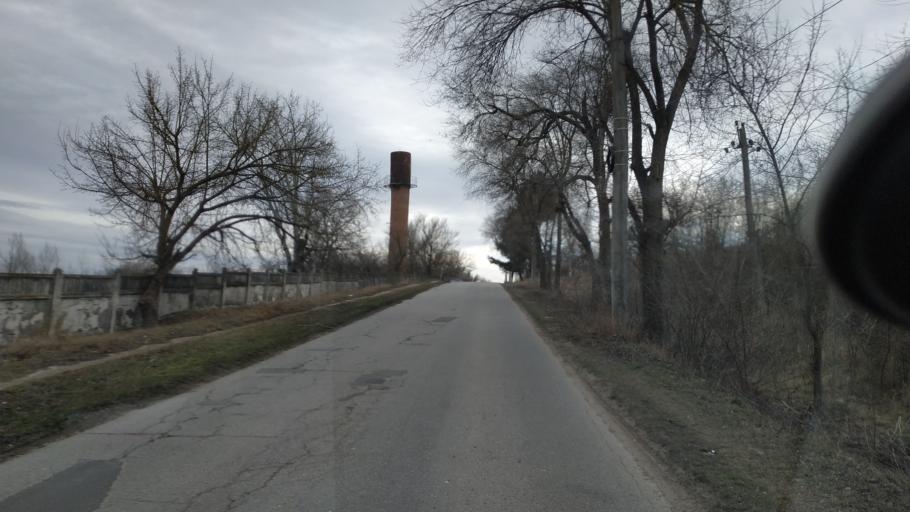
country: MD
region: Chisinau
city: Vadul lui Voda
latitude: 47.0996
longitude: 29.0687
